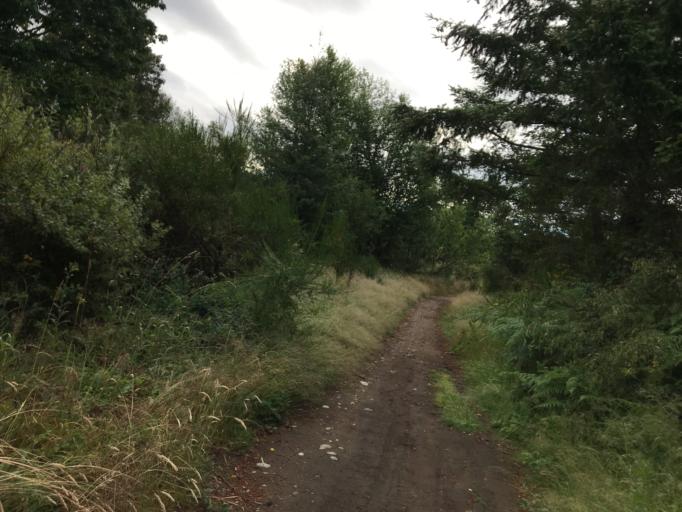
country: US
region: Washington
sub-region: King County
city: Ravensdale
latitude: 47.3444
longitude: -122.0060
